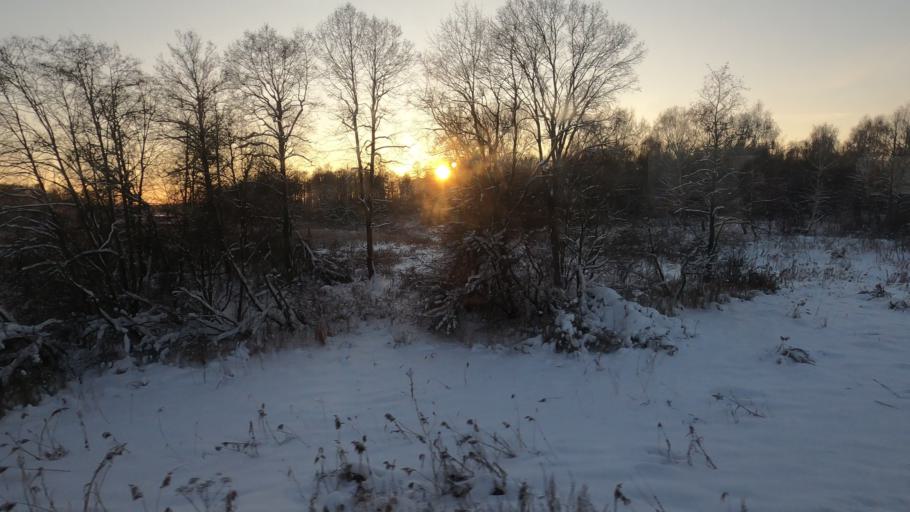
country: RU
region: Moskovskaya
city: Dmitrov
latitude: 56.3906
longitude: 37.5068
